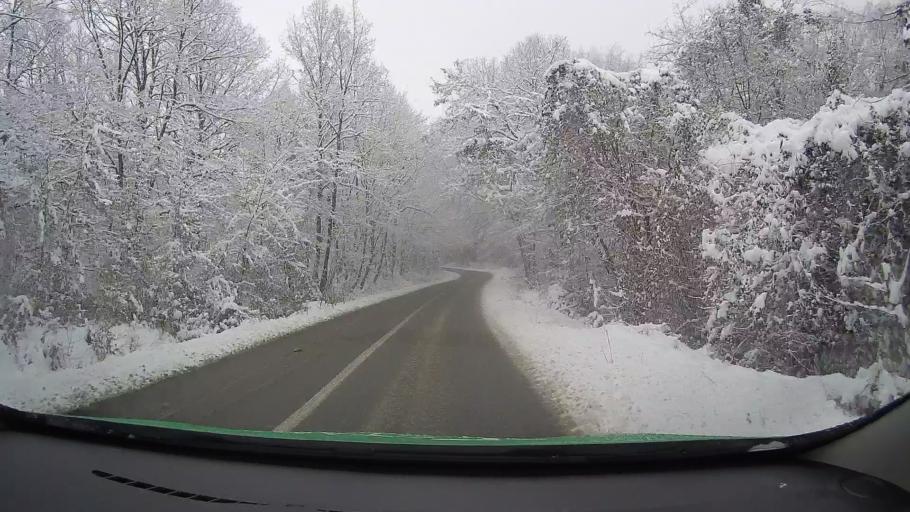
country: RO
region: Hunedoara
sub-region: Comuna Teliucu Inferior
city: Teliucu Inferior
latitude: 45.6783
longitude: 22.9130
